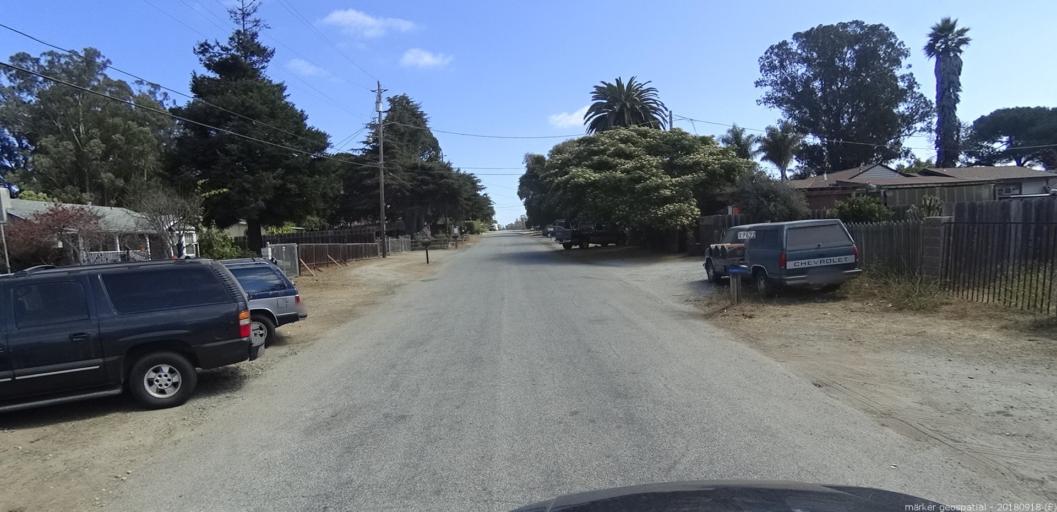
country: US
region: California
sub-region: Monterey County
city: Prunedale
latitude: 36.7740
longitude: -121.6675
